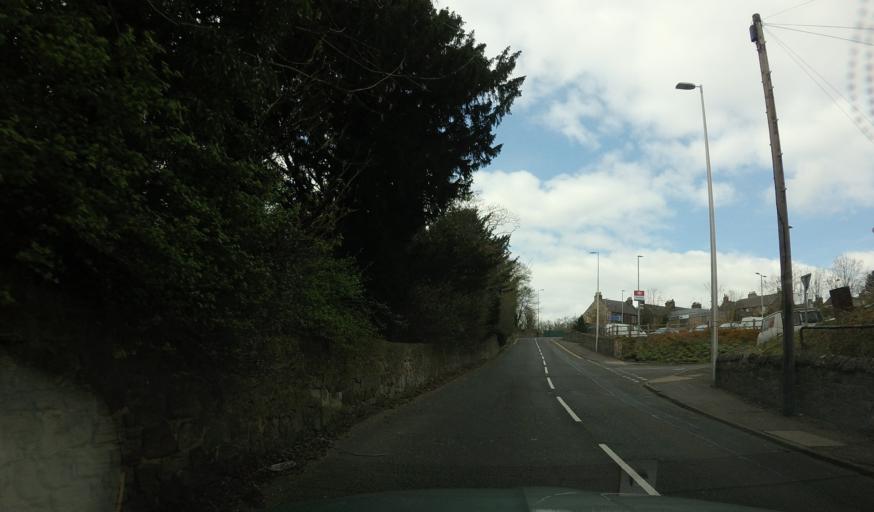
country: GB
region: Scotland
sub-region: Midlothian
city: Gorebridge
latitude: 55.8397
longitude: -3.0478
